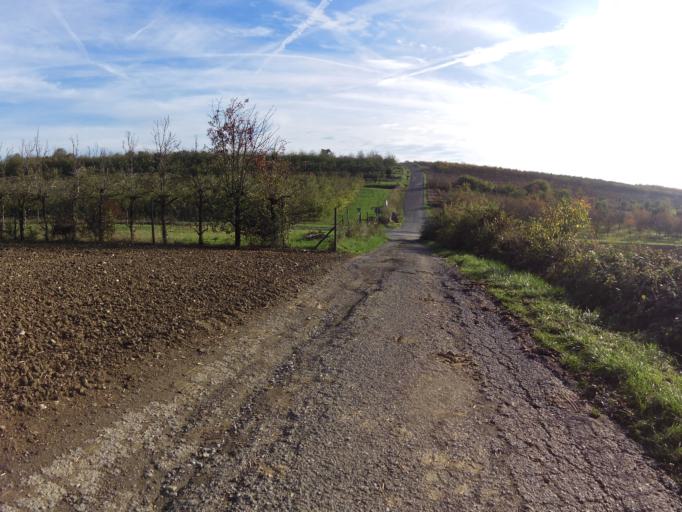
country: DE
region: Bavaria
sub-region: Regierungsbezirk Unterfranken
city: Sommerhausen
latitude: 49.7111
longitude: 10.0393
